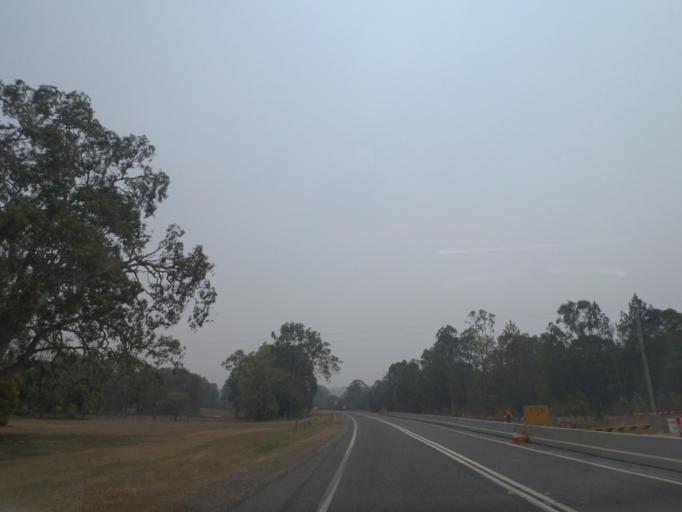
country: AU
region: New South Wales
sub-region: Clarence Valley
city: Maclean
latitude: -29.5492
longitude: 153.1559
